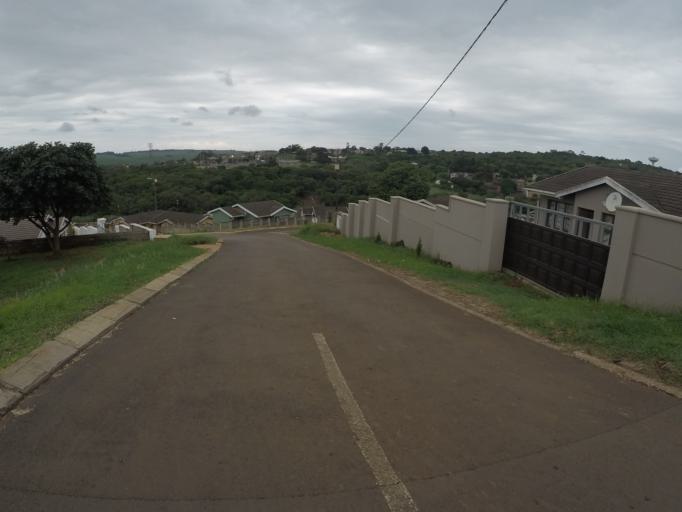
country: ZA
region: KwaZulu-Natal
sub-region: uThungulu District Municipality
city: Empangeni
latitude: -28.7710
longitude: 31.8694
